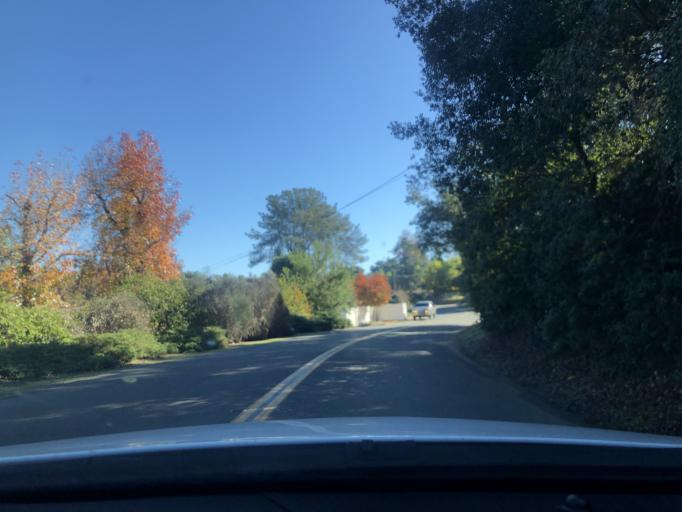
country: US
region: California
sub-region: San Diego County
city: El Cajon
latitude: 32.7754
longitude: -116.9417
